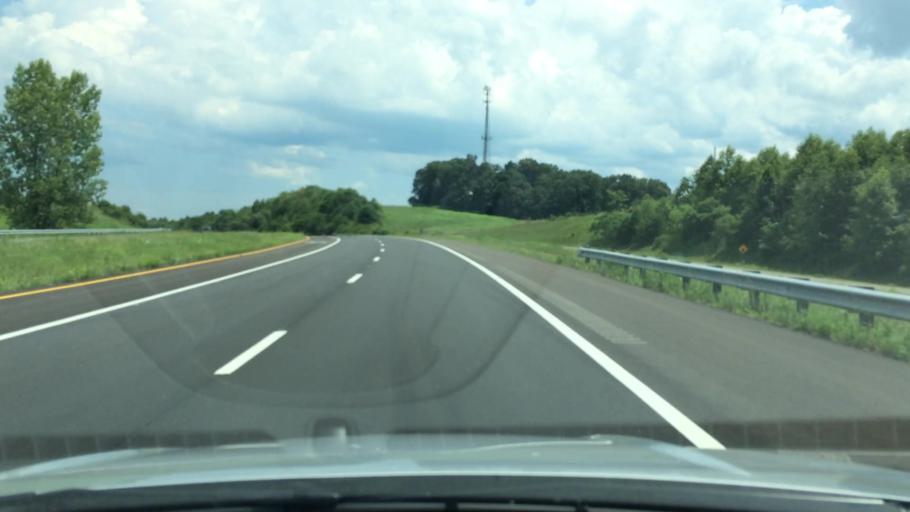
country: US
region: Tennessee
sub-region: Hamblen County
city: Morristown
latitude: 36.1723
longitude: -83.2297
